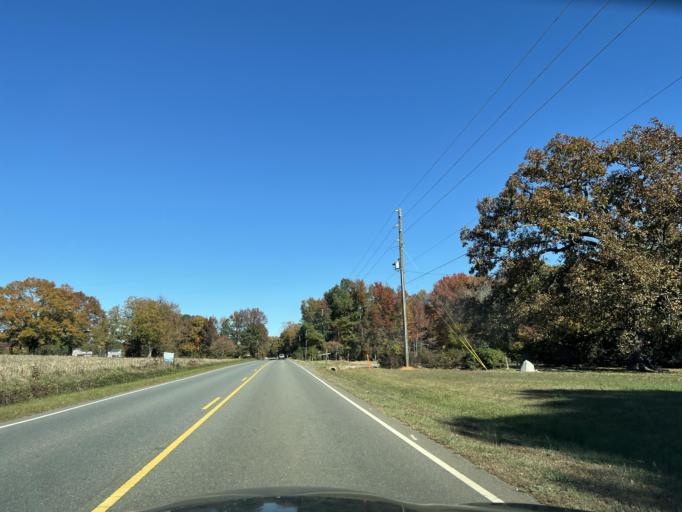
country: US
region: North Carolina
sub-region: Wake County
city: Fuquay-Varina
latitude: 35.6530
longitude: -78.7194
